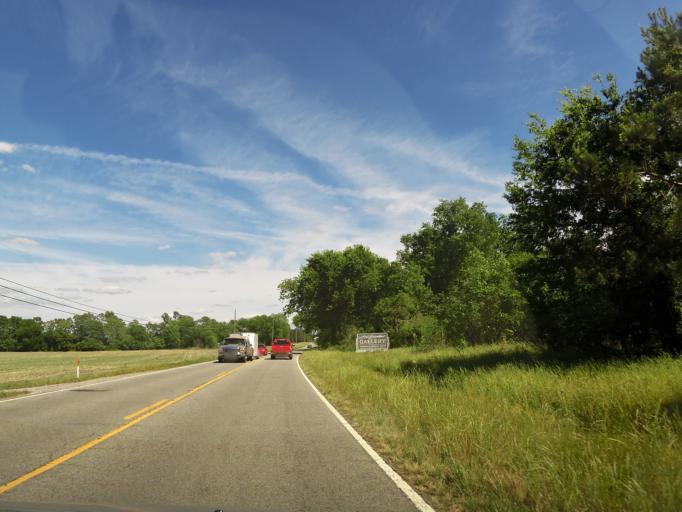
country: US
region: South Carolina
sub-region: Bamberg County
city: Denmark
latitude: 33.3345
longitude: -81.1609
